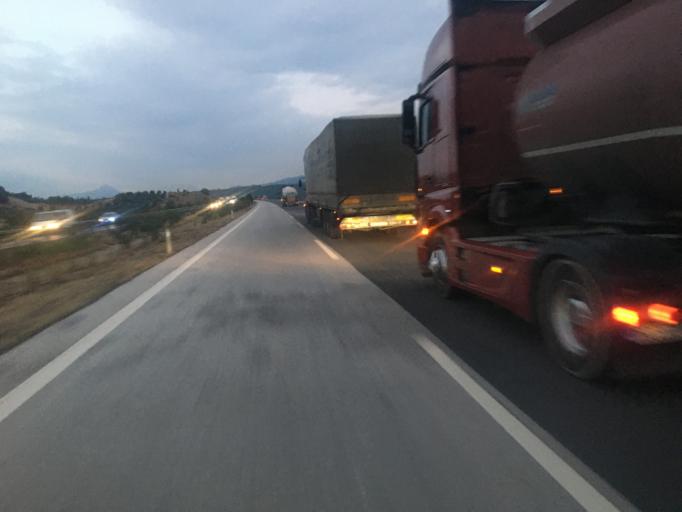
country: TR
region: Osmaniye
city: Kaypak
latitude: 37.1552
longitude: 36.3513
